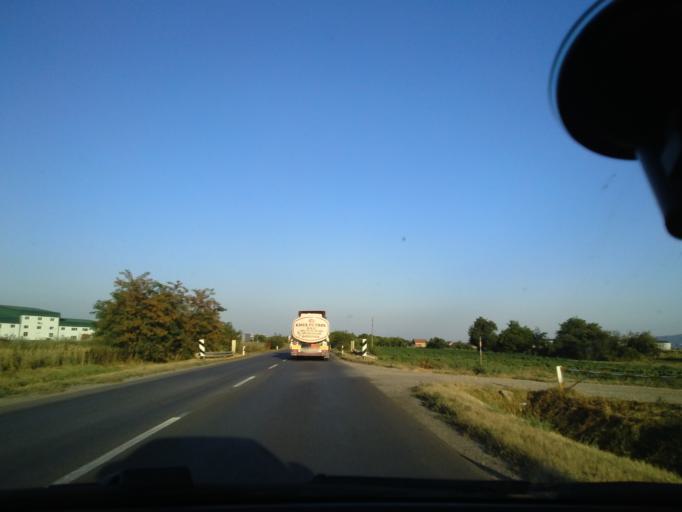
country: RS
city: Rumenka
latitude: 45.2859
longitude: 19.7614
